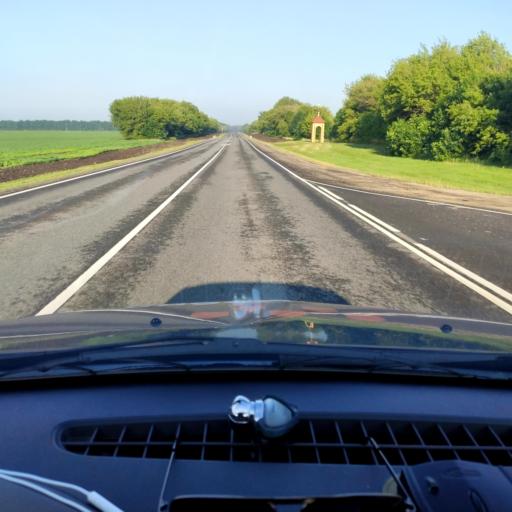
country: RU
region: Lipetsk
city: Izmalkovo
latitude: 52.4362
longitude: 37.8812
